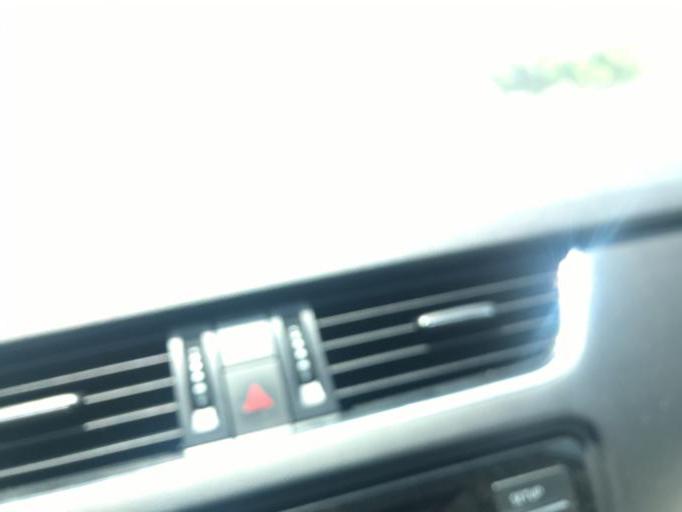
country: EG
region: Alexandria
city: Alexandria
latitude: 30.9780
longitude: 29.6601
